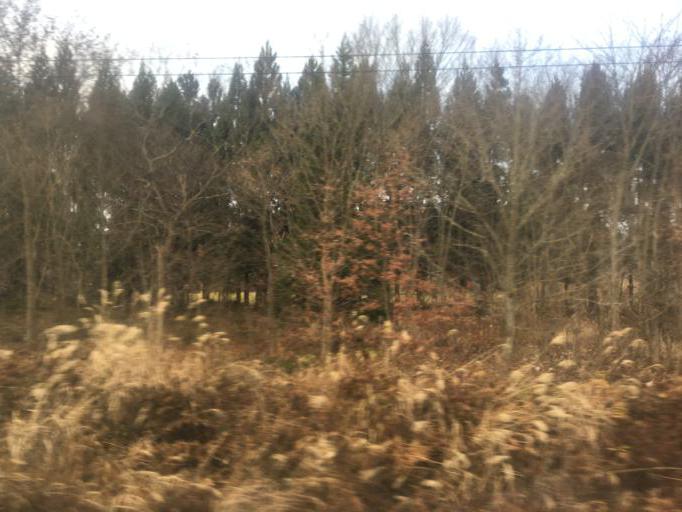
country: JP
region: Akita
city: Takanosu
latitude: 40.2391
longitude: 140.3839
